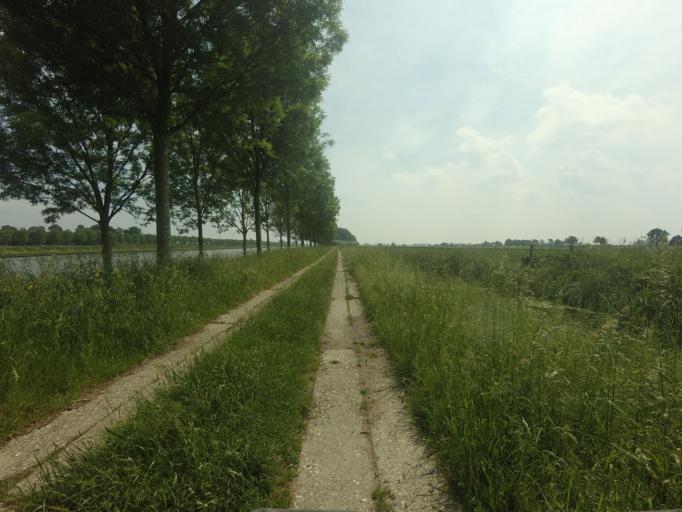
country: NL
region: Gelderland
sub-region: Gemeente Culemborg
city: Culemborg
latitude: 51.9864
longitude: 5.2502
